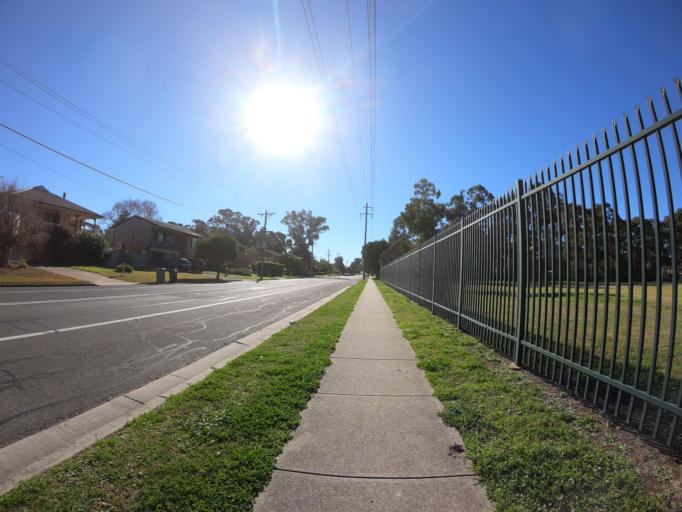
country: AU
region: New South Wales
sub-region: Hawkesbury
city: South Windsor
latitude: -33.6307
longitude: 150.7963
